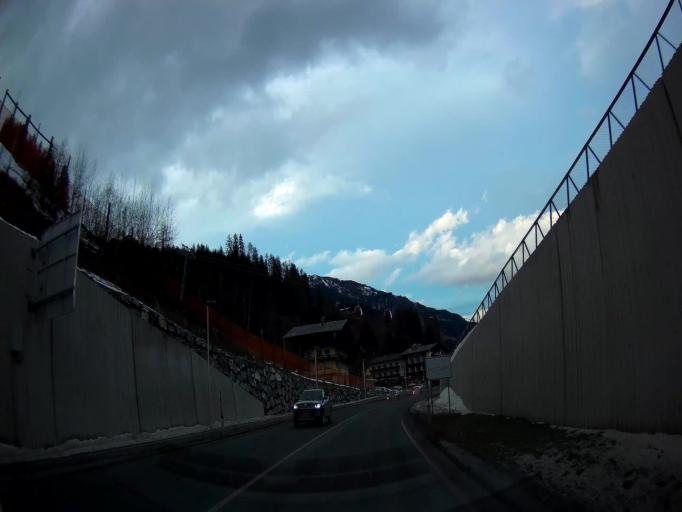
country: AT
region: Salzburg
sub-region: Politischer Bezirk Sankt Johann im Pongau
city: Bad Hofgastein
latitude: 47.1668
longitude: 13.0980
